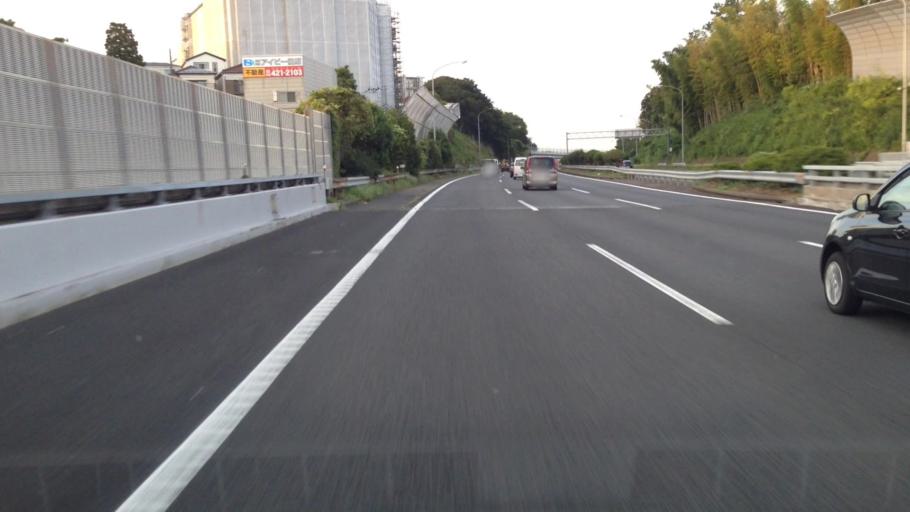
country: JP
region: Tokyo
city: Chofugaoka
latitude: 35.5653
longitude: 139.6105
